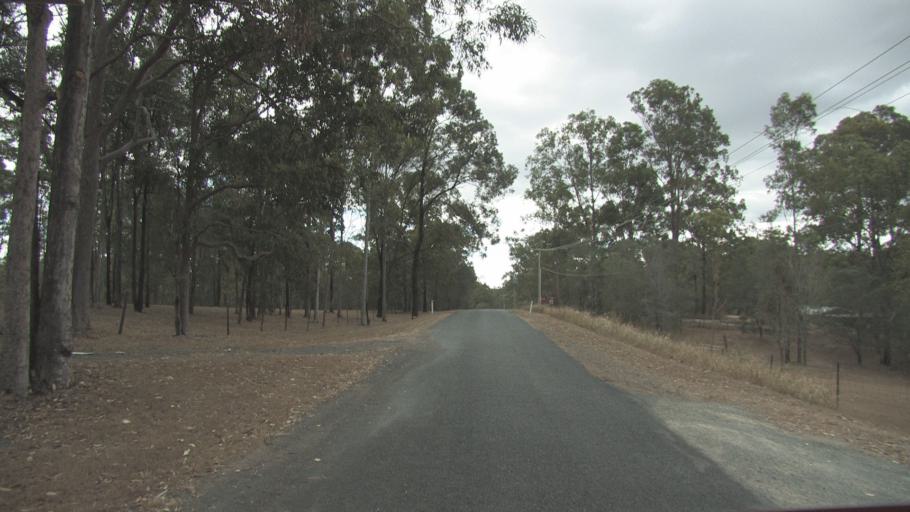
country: AU
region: Queensland
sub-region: Logan
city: Cedar Vale
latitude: -27.8853
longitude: 153.0341
